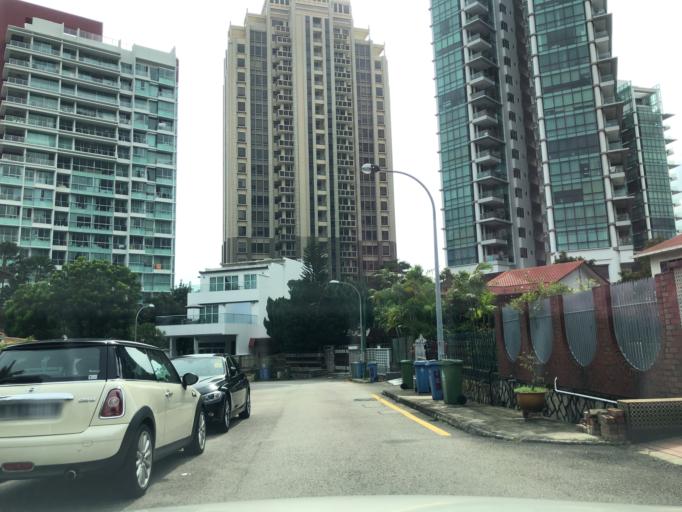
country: SG
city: Singapore
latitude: 1.3017
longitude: 103.8251
